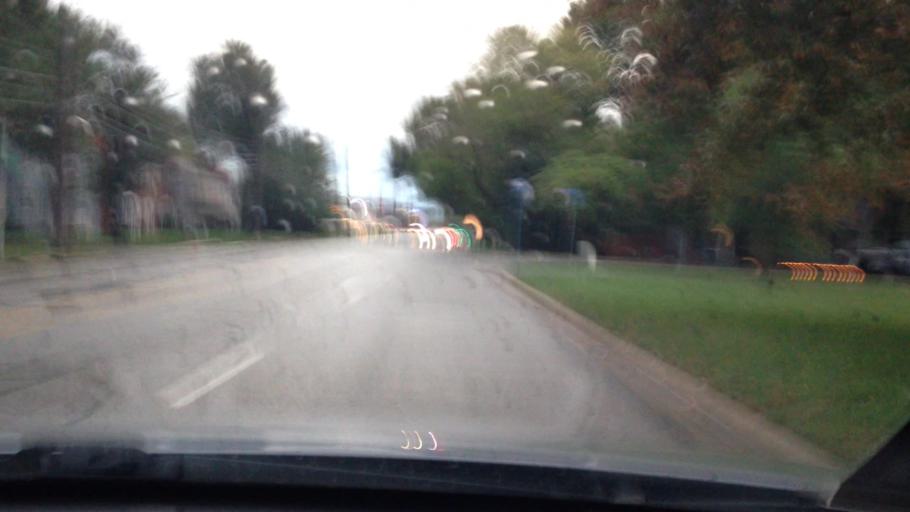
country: US
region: Kansas
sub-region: Johnson County
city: Leawood
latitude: 38.9881
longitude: -94.6080
